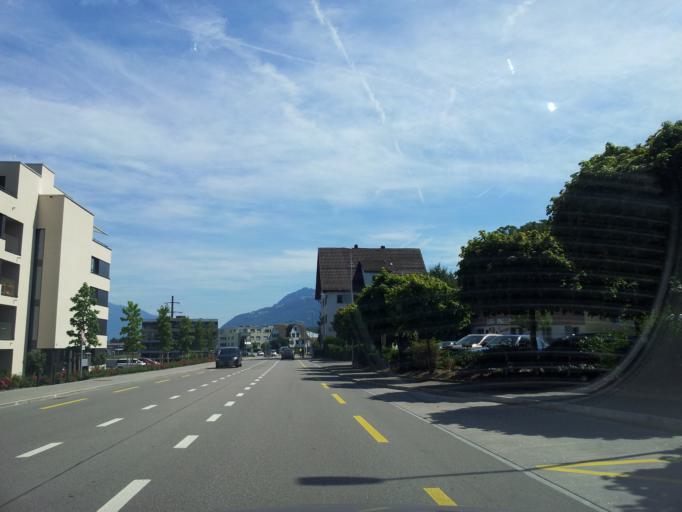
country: CH
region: Schwyz
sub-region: Bezirk March
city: Altendorf
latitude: 47.1907
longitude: 8.8359
